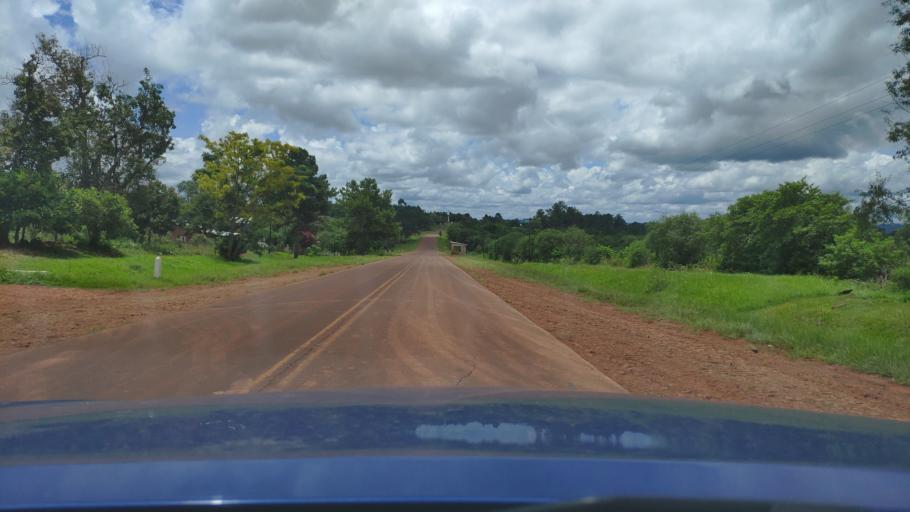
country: AR
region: Misiones
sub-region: Departamento de San Javier
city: San Javier
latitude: -27.8614
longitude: -55.2544
